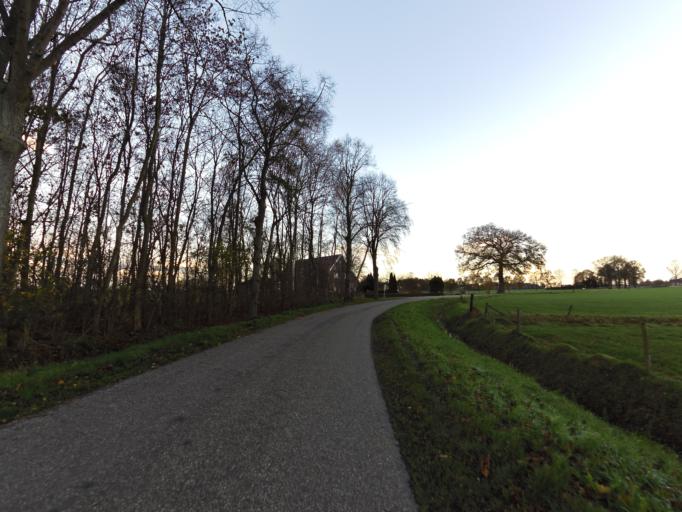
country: NL
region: Gelderland
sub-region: Oude IJsselstreek
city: Gendringen
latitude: 51.8510
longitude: 6.3647
